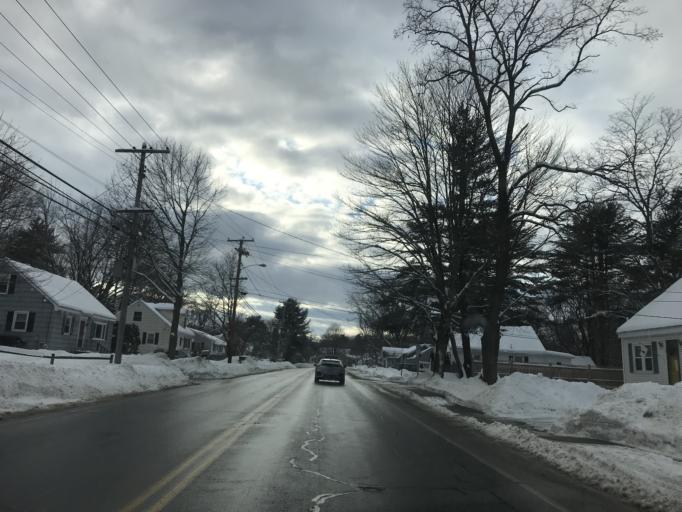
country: US
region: Maine
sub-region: Cumberland County
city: Westbrook
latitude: 43.6956
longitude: -70.3472
